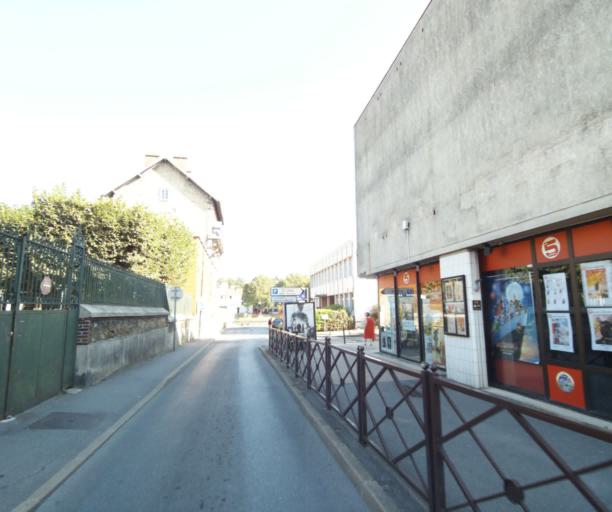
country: FR
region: Ile-de-France
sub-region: Departement de Seine-et-Marne
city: Thorigny-sur-Marne
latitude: 48.8794
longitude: 2.7061
